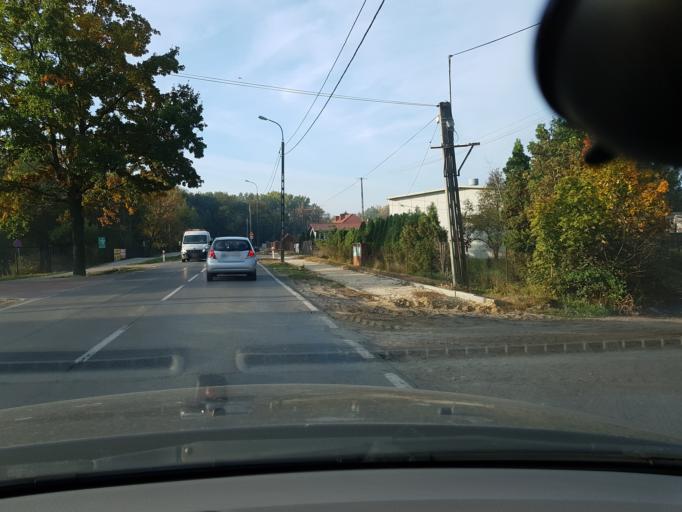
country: PL
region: Masovian Voivodeship
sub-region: Powiat otwocki
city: Jozefow
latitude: 52.1780
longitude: 21.2968
